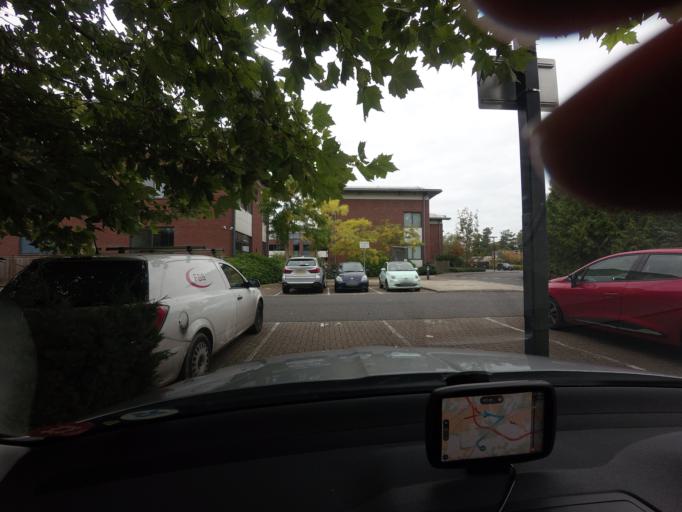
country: GB
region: England
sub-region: Surrey
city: Byfleet
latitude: 51.3417
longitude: -0.4633
